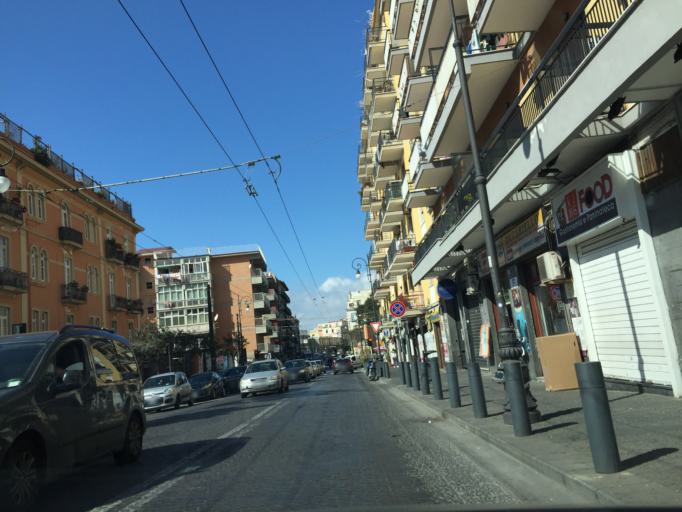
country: IT
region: Campania
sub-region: Provincia di Napoli
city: Portici
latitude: 40.8176
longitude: 14.3316
